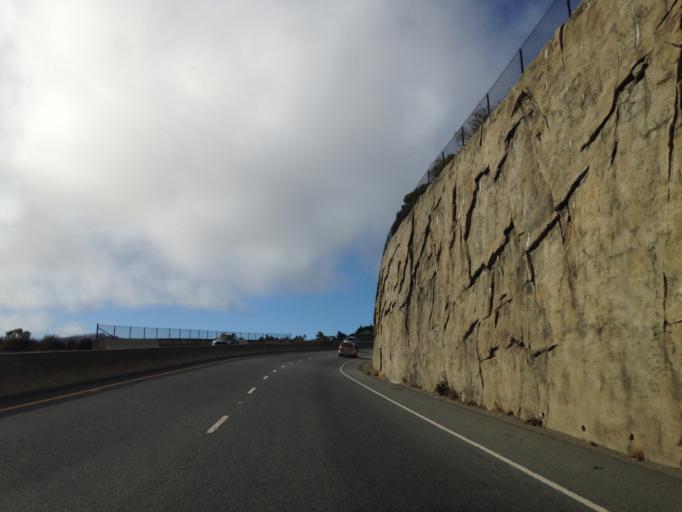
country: US
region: California
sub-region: San Mateo County
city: Highlands-Baywood Park
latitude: 37.4877
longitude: -122.3705
